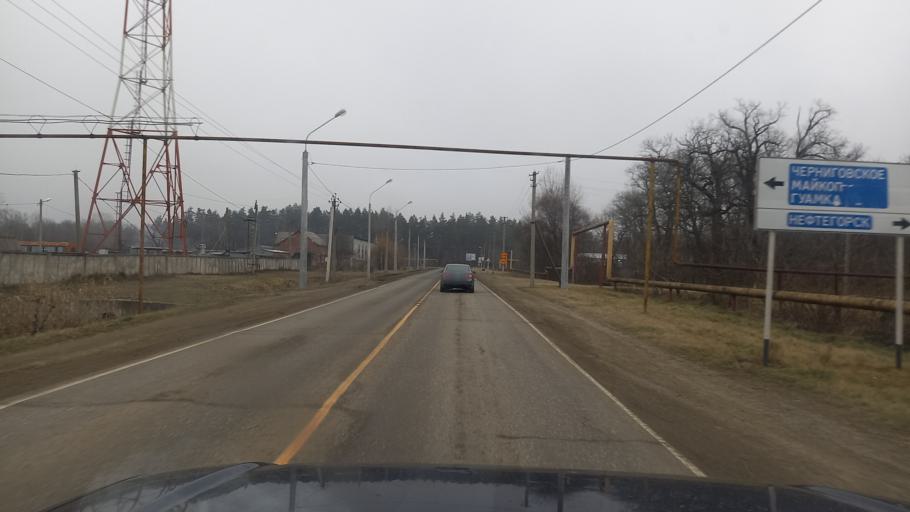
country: RU
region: Krasnodarskiy
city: Apsheronsk
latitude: 44.4375
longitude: 39.7607
